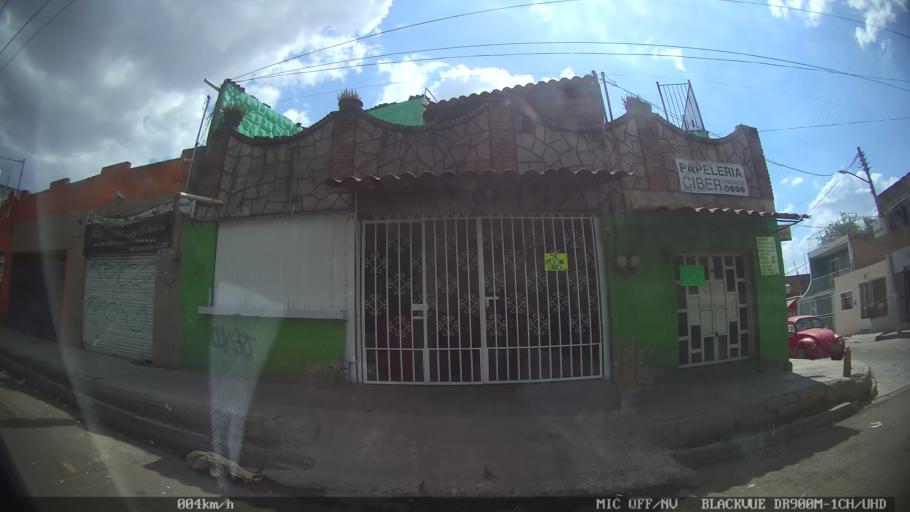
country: MX
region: Jalisco
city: Tlaquepaque
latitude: 20.6851
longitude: -103.2642
